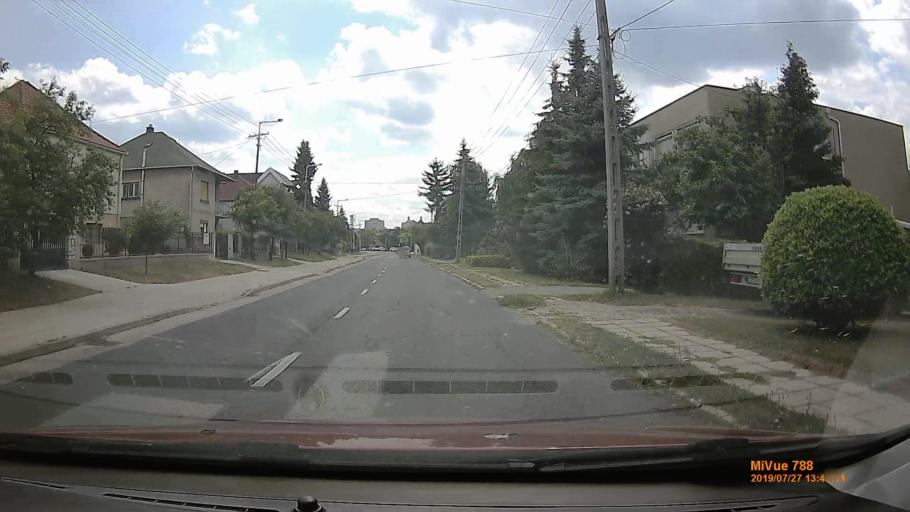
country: HU
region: Veszprem
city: Ajka
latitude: 47.1162
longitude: 17.5636
